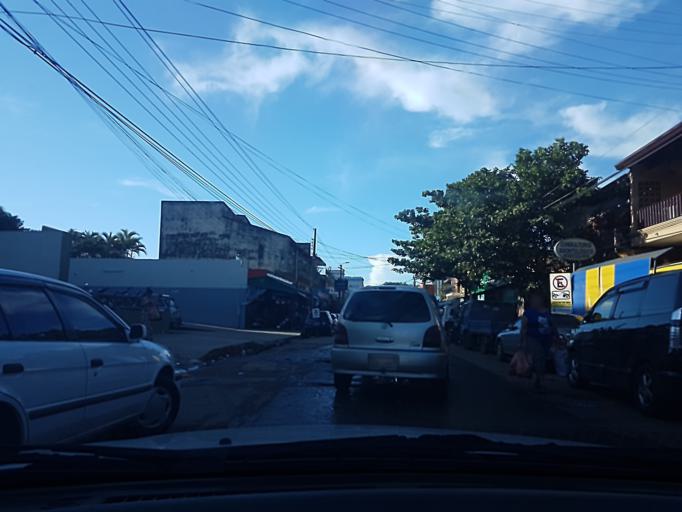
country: PY
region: Central
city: San Lorenzo
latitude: -25.2707
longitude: -57.4879
